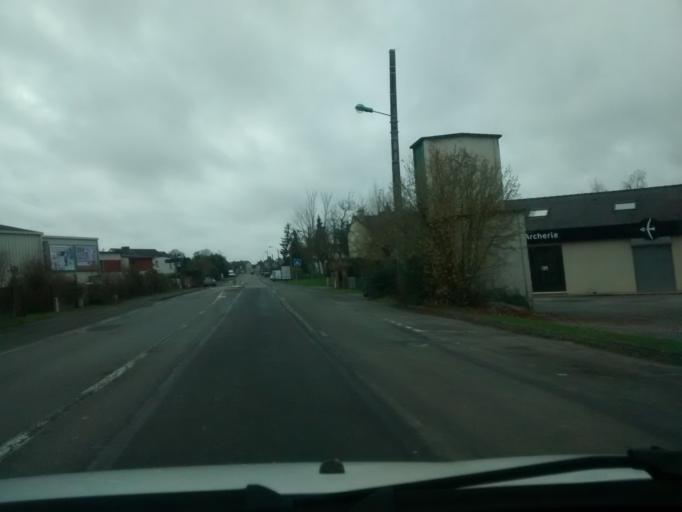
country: FR
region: Brittany
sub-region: Departement d'Ille-et-Vilaine
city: Fouillard
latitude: 48.1625
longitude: -1.5830
